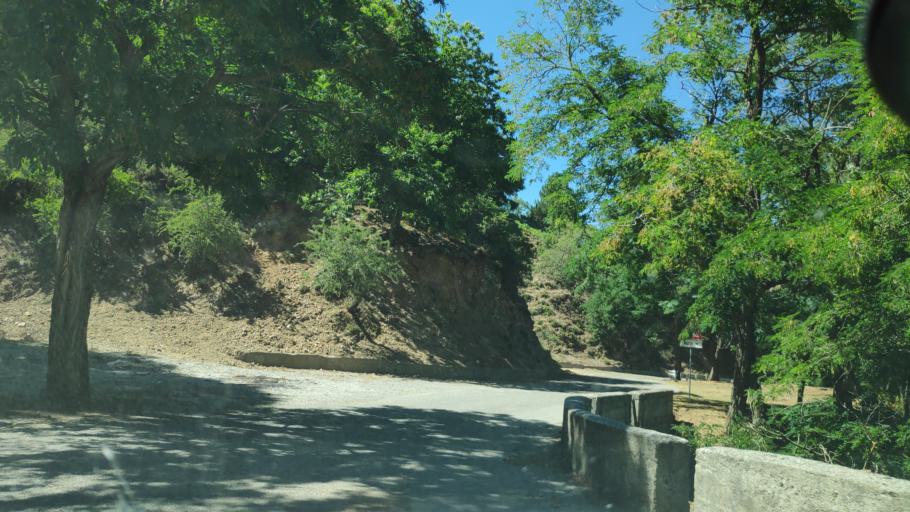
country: IT
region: Calabria
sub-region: Provincia di Reggio Calabria
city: Africo Vecchio
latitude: 38.0386
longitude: 15.9506
